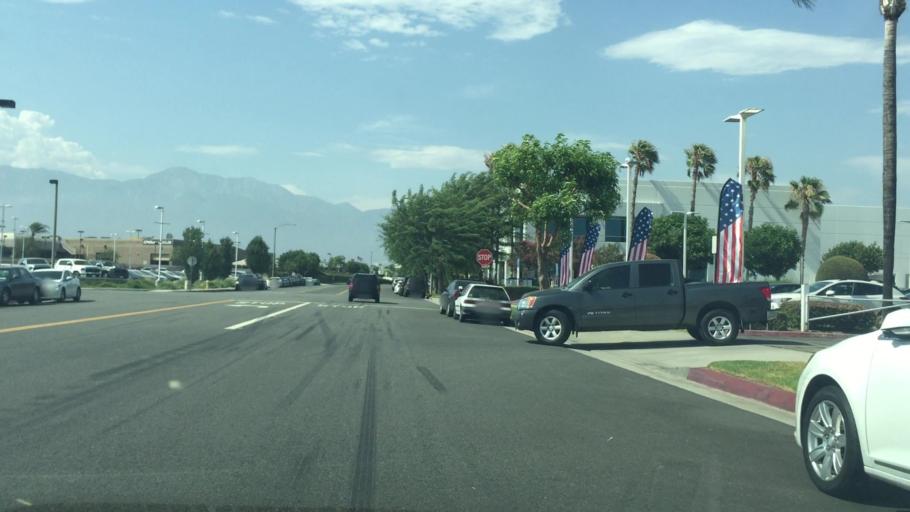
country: US
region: California
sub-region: Riverside County
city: Mira Loma
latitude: 34.0522
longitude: -117.5447
